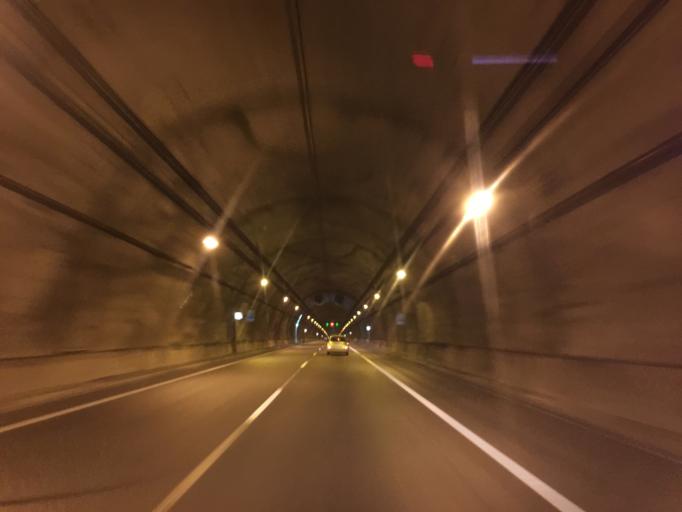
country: ES
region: Asturias
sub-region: Province of Asturias
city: Arriba
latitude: 43.4668
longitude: -5.5234
